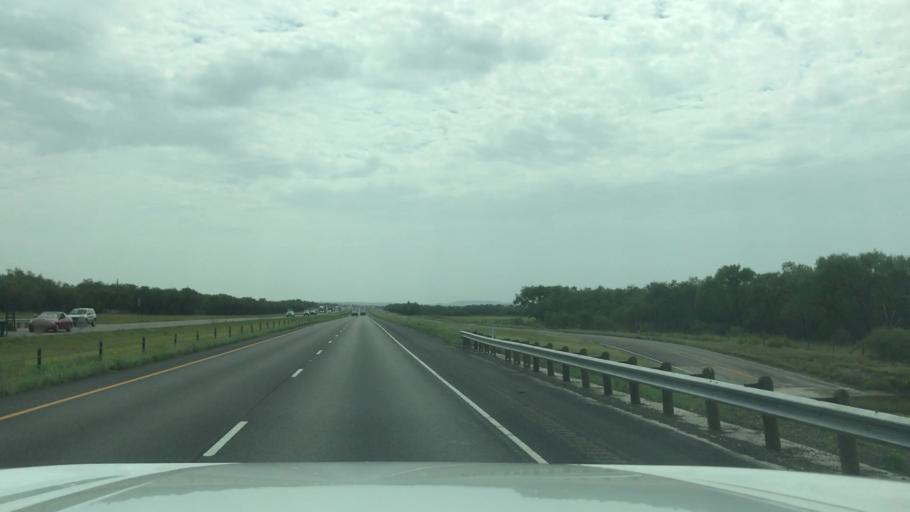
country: US
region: Texas
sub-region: Callahan County
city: Baird
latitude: 32.3881
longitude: -99.3182
